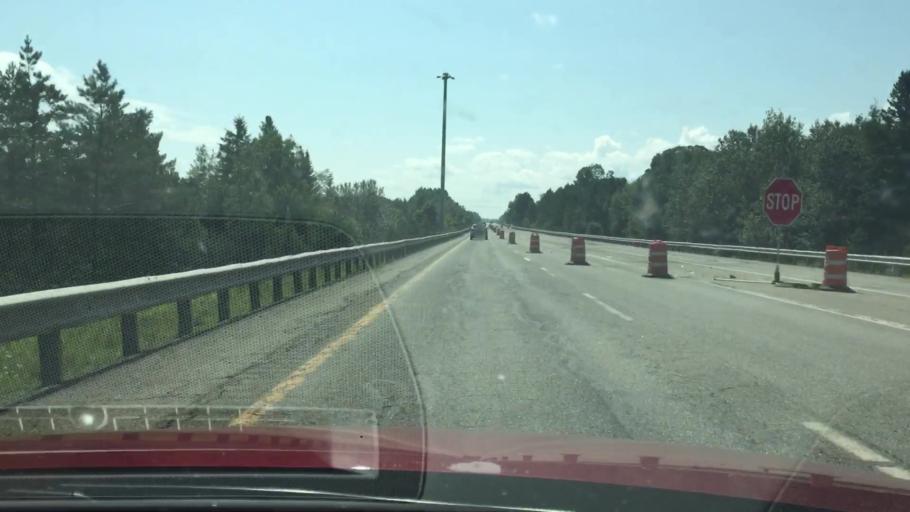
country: US
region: Maine
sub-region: Penobscot County
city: Patten
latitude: 45.8701
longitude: -68.4150
